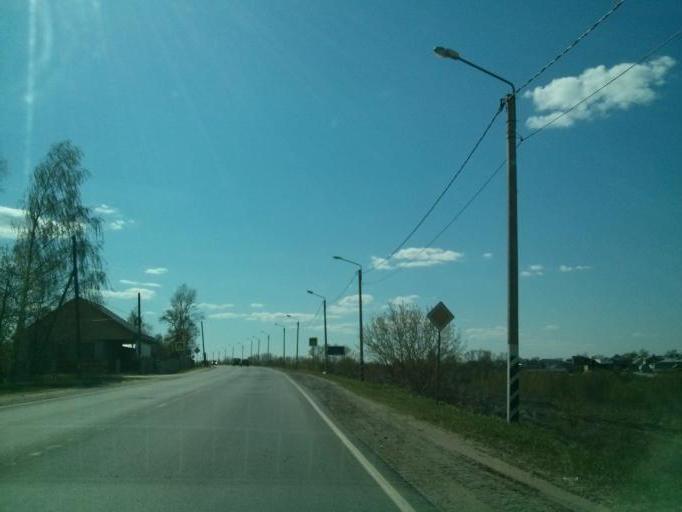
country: RU
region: Nizjnij Novgorod
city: Pavlovo
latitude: 55.9528
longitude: 43.1195
